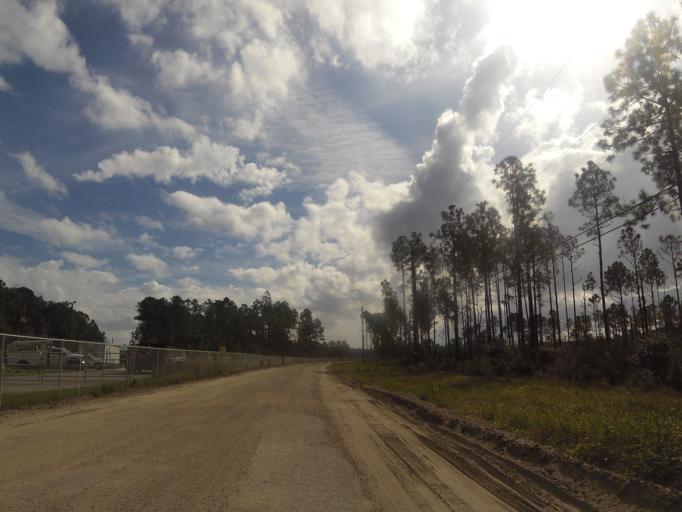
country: US
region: Florida
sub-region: Saint Johns County
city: Villano Beach
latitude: 29.9915
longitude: -81.3893
